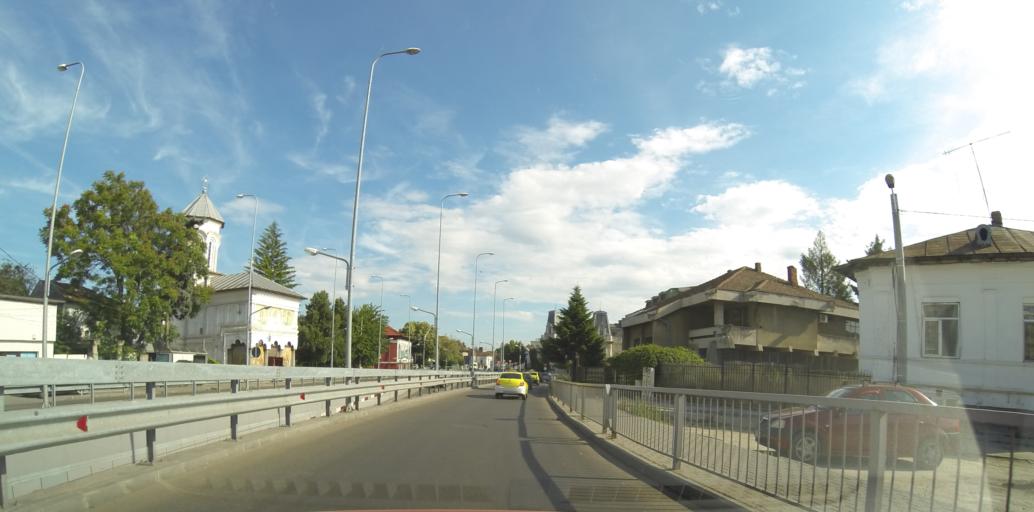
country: RO
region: Dolj
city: Craiova
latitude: 44.3165
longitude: 23.8014
